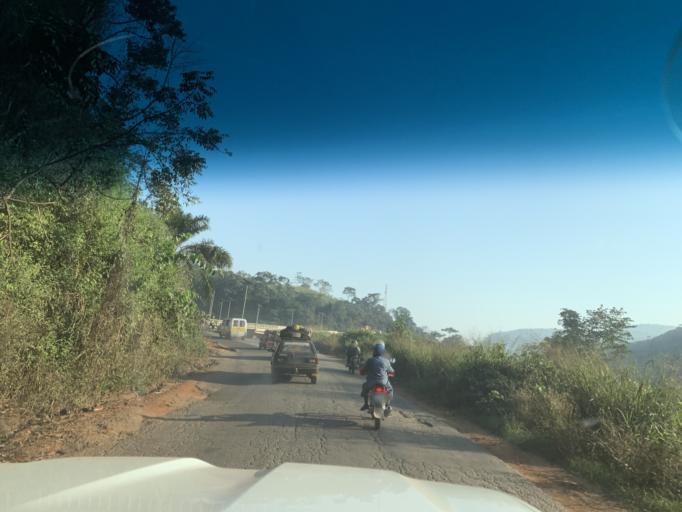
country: GN
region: Kindia
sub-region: Coyah
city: Coyah
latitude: 9.7476
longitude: -13.3614
